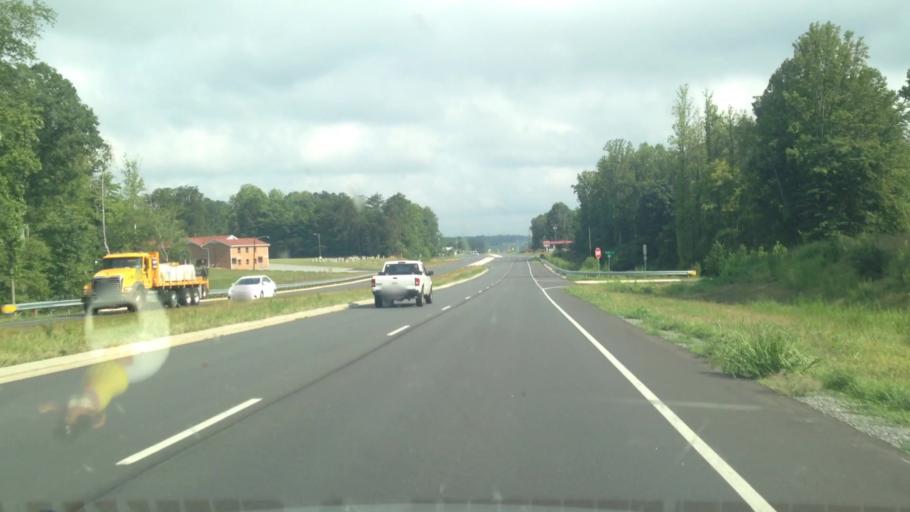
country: US
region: North Carolina
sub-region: Guilford County
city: Summerfield
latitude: 36.2116
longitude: -79.9057
